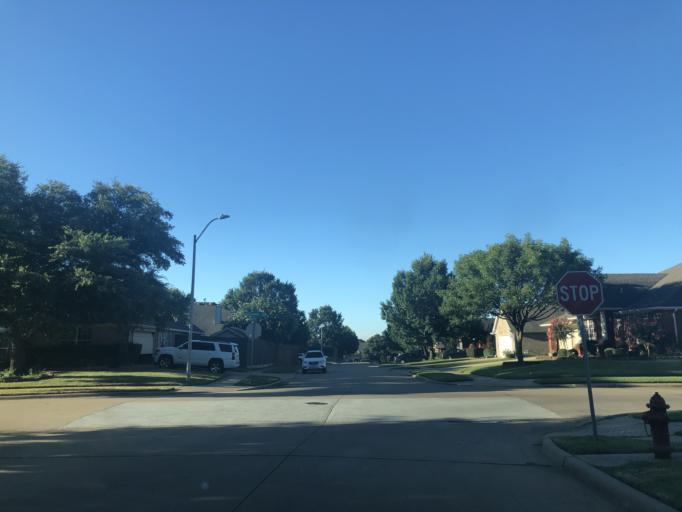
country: US
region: Texas
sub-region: Dallas County
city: Grand Prairie
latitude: 32.6626
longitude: -96.9985
